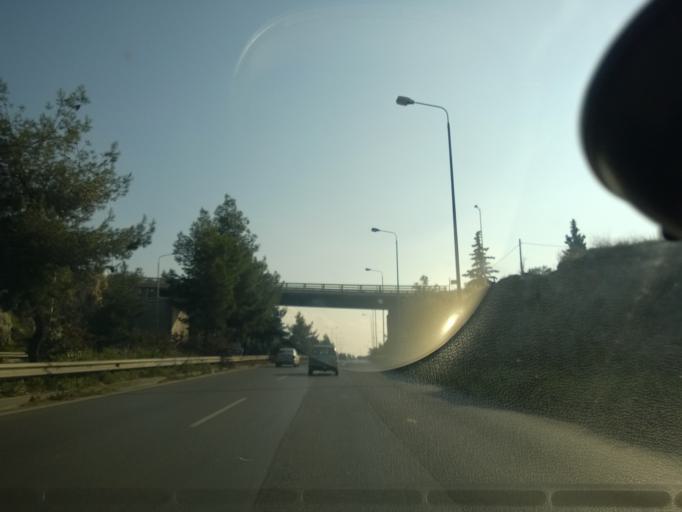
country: GR
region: Central Macedonia
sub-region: Nomos Thessalonikis
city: Agios Pavlos
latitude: 40.6432
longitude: 22.9694
